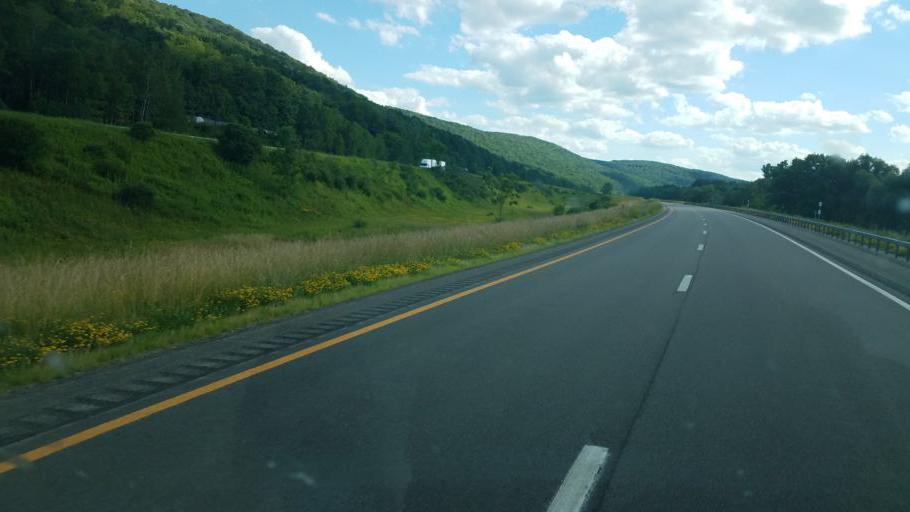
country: US
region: New York
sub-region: Allegany County
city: Cuba
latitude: 42.2092
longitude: -78.3250
